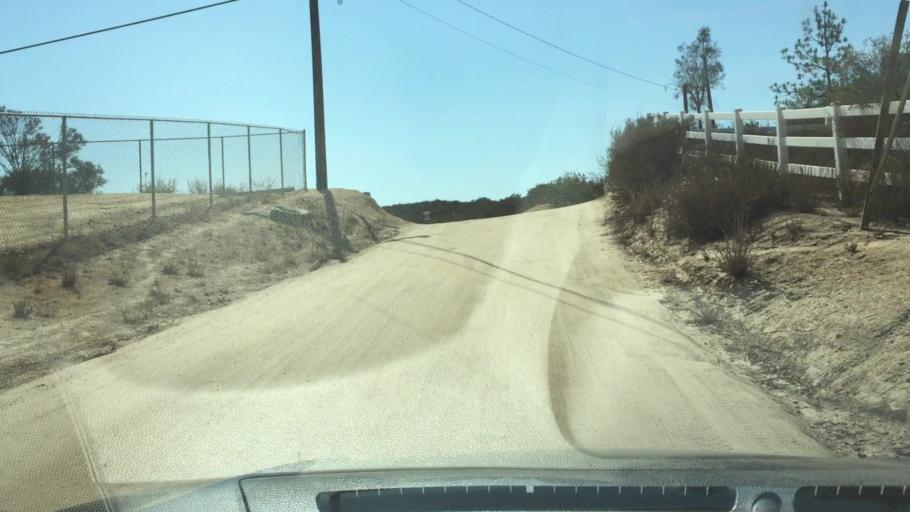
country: US
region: California
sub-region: San Diego County
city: Alpine
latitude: 32.7556
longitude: -116.7568
